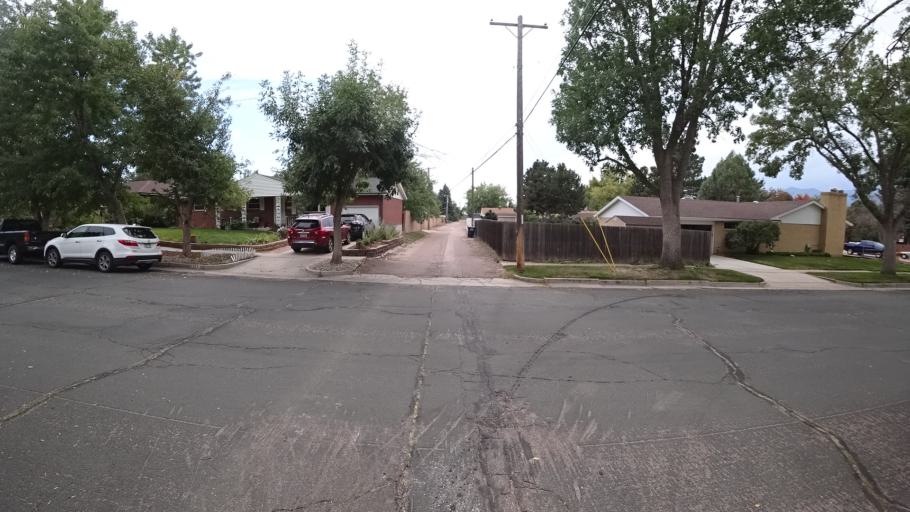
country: US
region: Colorado
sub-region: El Paso County
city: Colorado Springs
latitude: 38.8626
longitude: -104.7855
